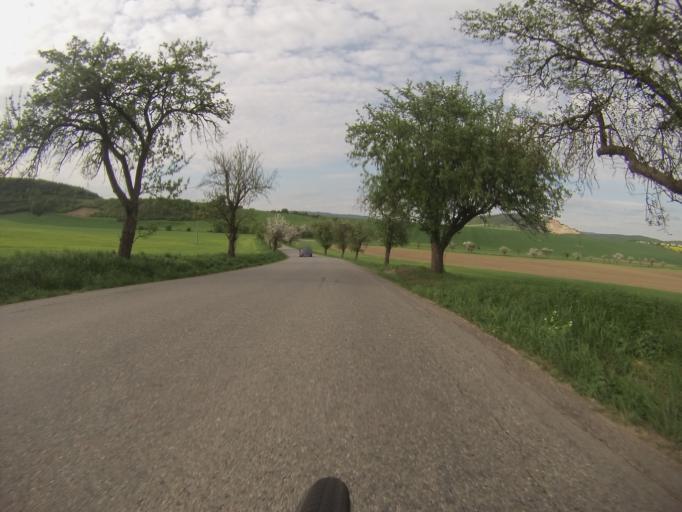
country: CZ
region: South Moravian
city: Cebin
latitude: 49.3027
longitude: 16.4604
